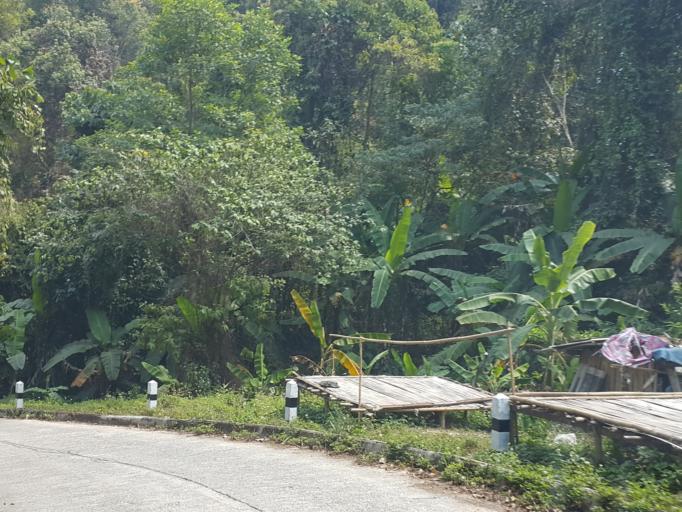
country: TH
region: Lampang
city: Mueang Pan
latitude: 18.8271
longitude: 99.4161
